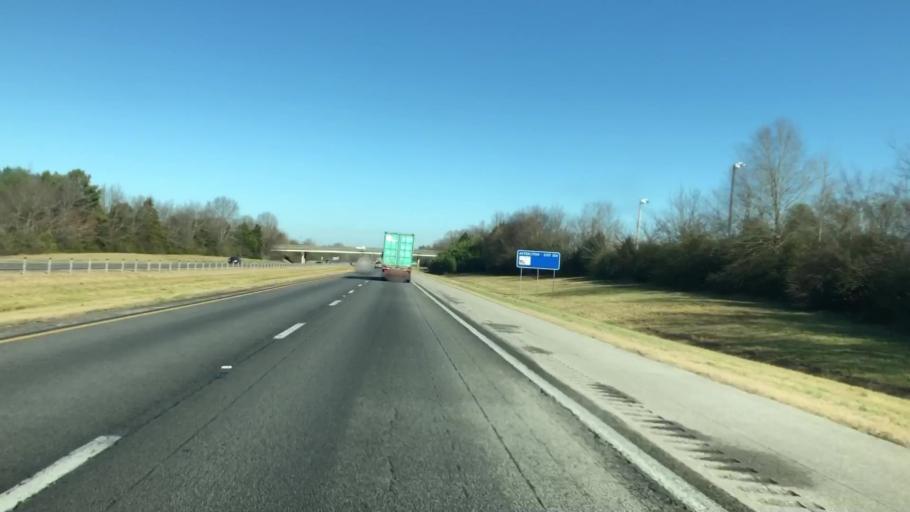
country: US
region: Alabama
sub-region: Limestone County
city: Athens
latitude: 34.8080
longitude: -86.9386
